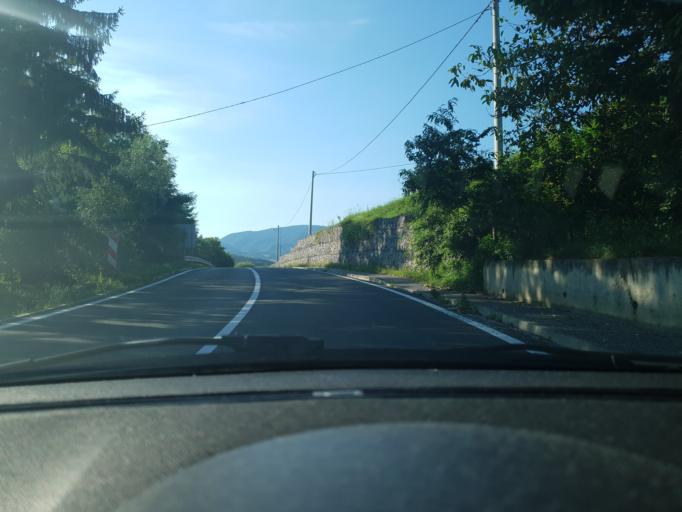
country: HR
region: Krapinsko-Zagorska
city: Mihovljan
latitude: 46.1332
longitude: 15.9384
